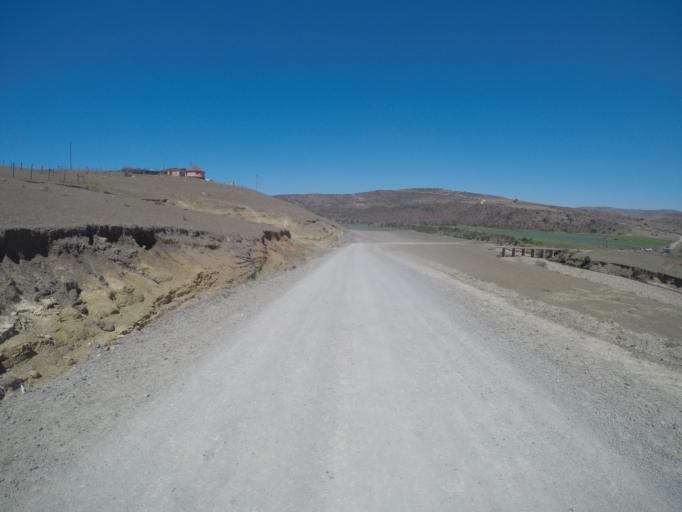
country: ZA
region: Eastern Cape
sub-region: OR Tambo District Municipality
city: Mthatha
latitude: -31.8673
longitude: 28.8720
